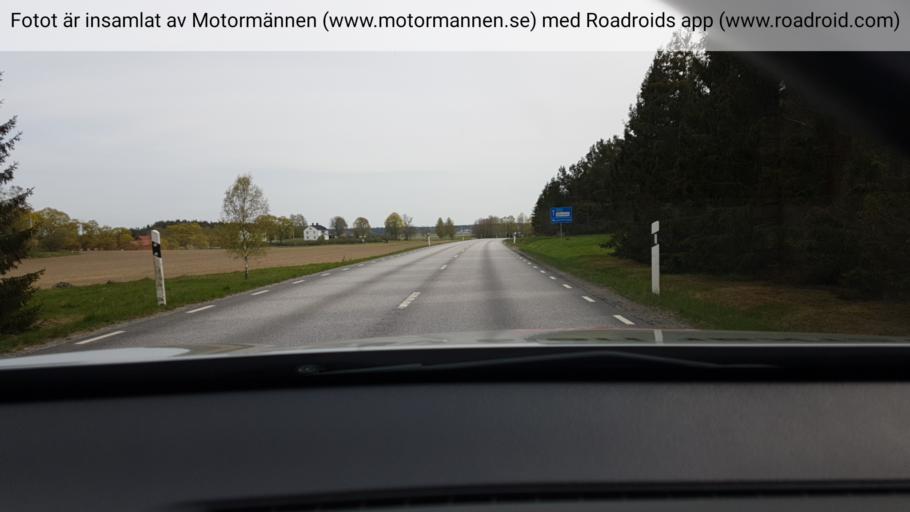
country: SE
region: Stockholm
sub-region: Vallentuna Kommun
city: Vallentuna
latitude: 59.6973
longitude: 18.0444
